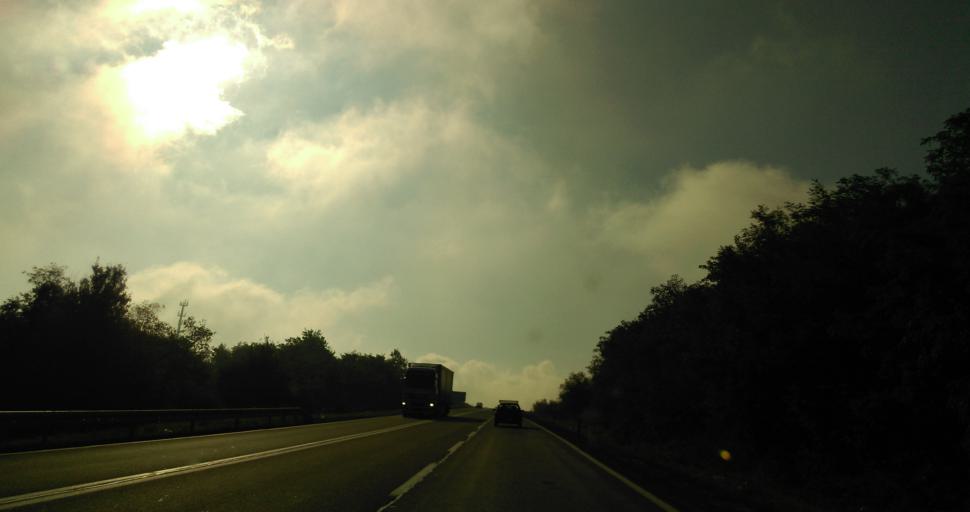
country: RS
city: Rusanj
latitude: 44.6635
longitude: 20.4273
